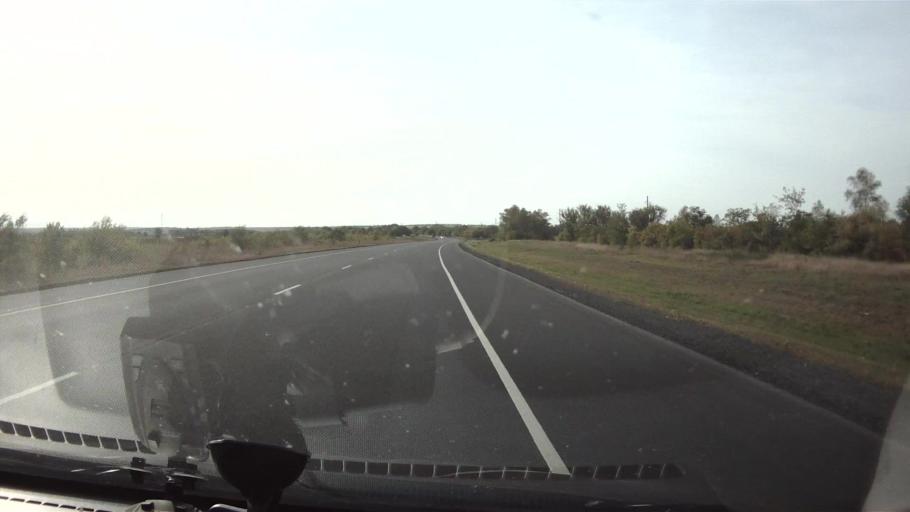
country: RU
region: Saratov
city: Yelshanka
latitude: 51.8282
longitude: 46.2474
